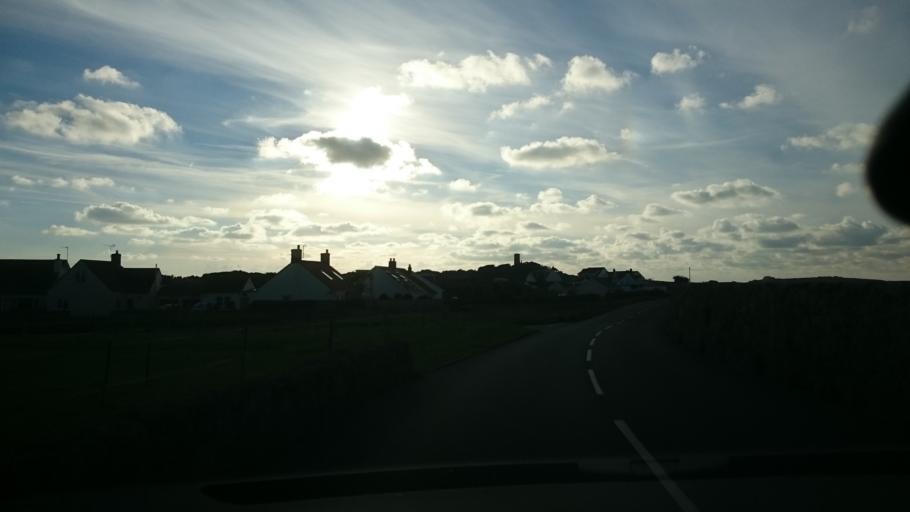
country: GG
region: St Peter Port
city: Saint Peter Port
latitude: 49.4603
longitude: -2.6435
